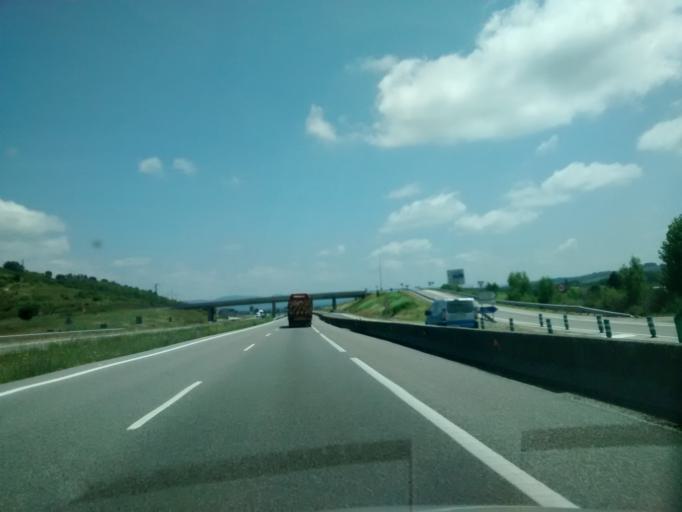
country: ES
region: Castille and Leon
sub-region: Provincia de Leon
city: Congosto
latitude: 42.5920
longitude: -6.5176
